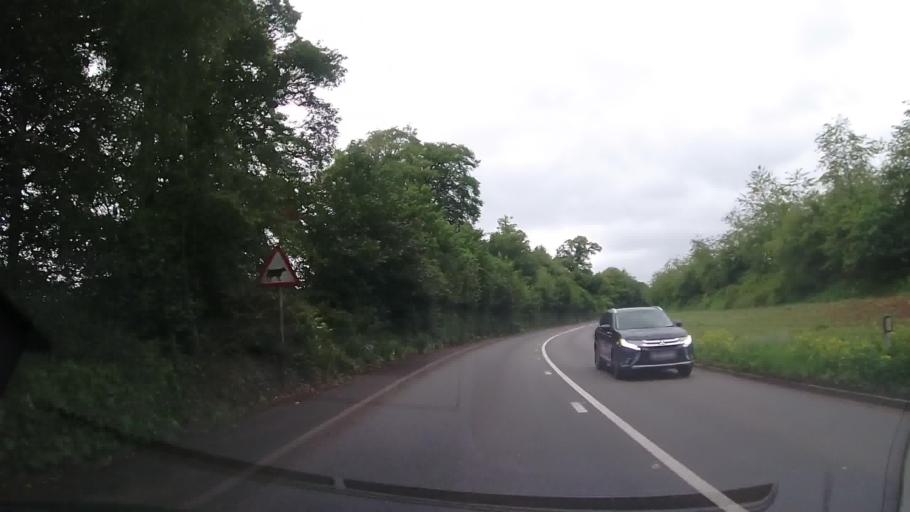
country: GB
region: England
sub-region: Staffordshire
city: Standon
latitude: 52.9688
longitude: -2.2790
